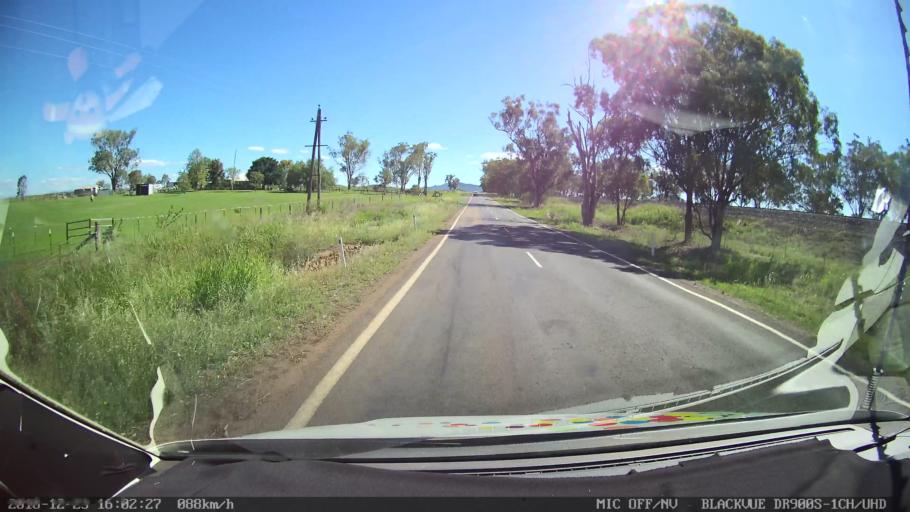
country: AU
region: New South Wales
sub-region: Tamworth Municipality
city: Phillip
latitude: -31.2324
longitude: 150.8089
